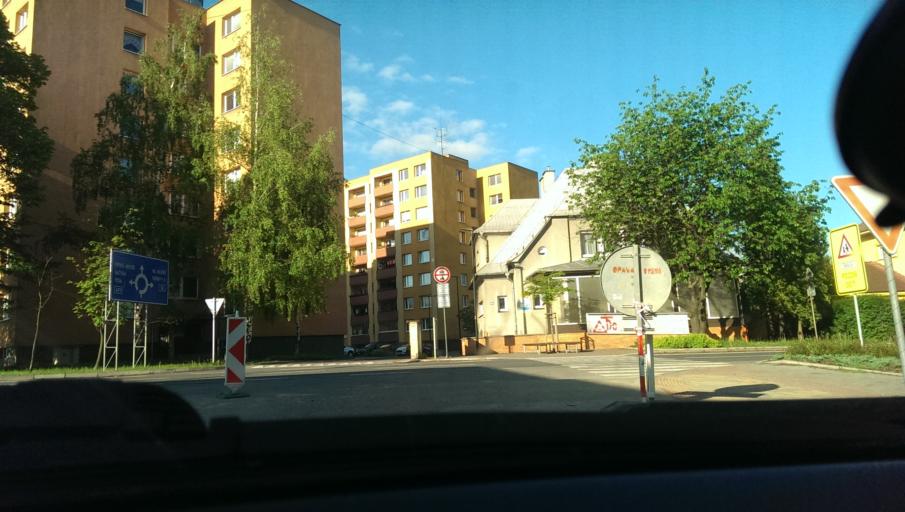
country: CZ
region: Moravskoslezsky
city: Frenstat pod Radhostem
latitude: 49.5460
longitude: 18.2105
